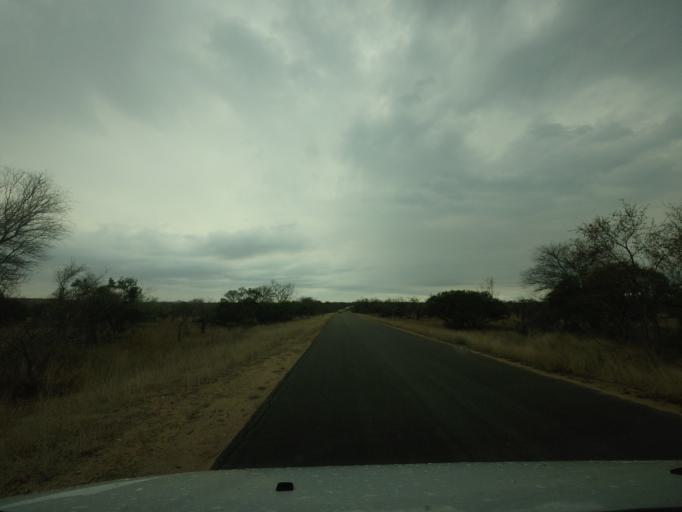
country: ZA
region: Limpopo
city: Thulamahashi
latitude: -24.4697
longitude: 31.4357
